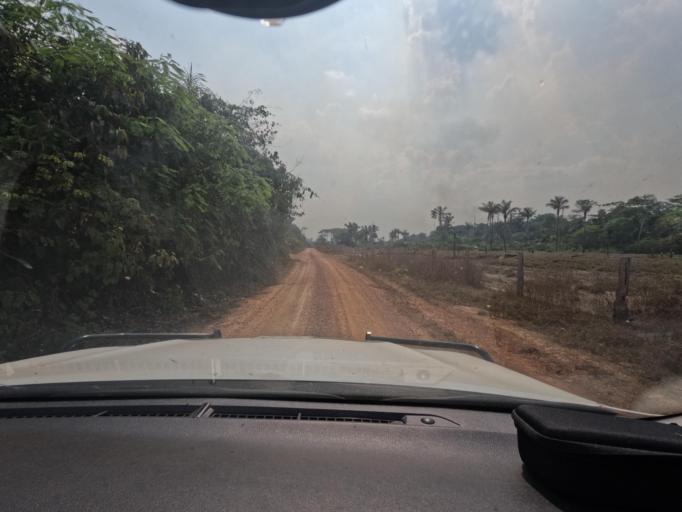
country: BR
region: Rondonia
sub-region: Porto Velho
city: Porto Velho
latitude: -8.7728
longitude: -63.1826
